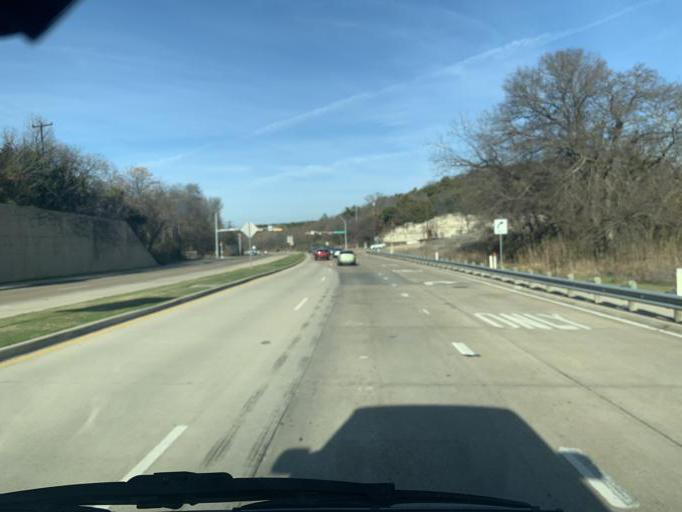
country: US
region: Texas
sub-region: Dallas County
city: Cedar Hill
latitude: 32.6097
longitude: -96.9562
